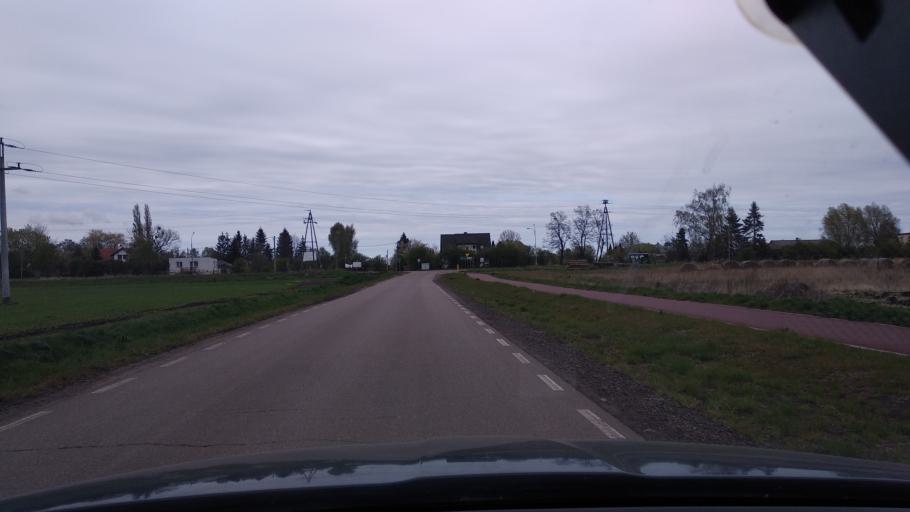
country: PL
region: Pomeranian Voivodeship
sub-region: Powiat gdanski
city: Pruszcz Gdanski
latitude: 54.2760
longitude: 18.6613
